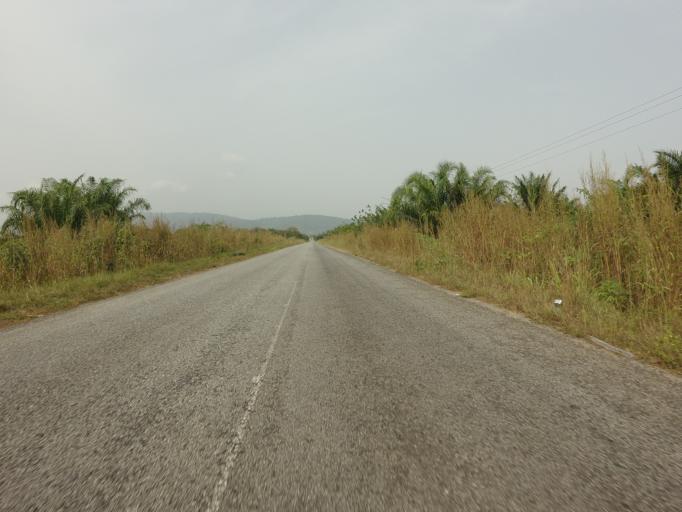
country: GH
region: Volta
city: Ho
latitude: 6.5742
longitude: 0.3416
